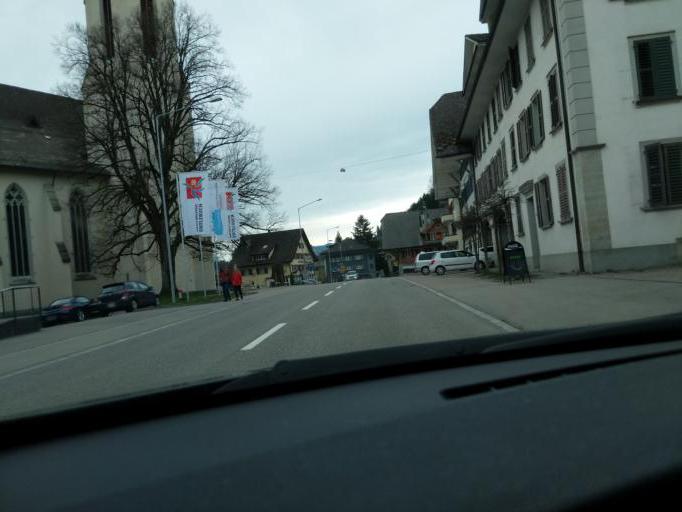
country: CH
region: Lucerne
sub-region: Entlebuch District
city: Escholzmatt
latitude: 46.9146
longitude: 7.9349
